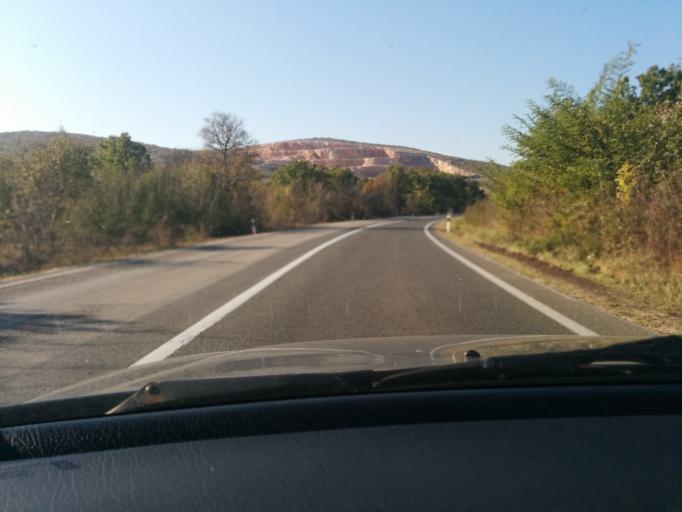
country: HR
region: Splitsko-Dalmatinska
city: Brnaze
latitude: 43.6432
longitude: 16.6189
